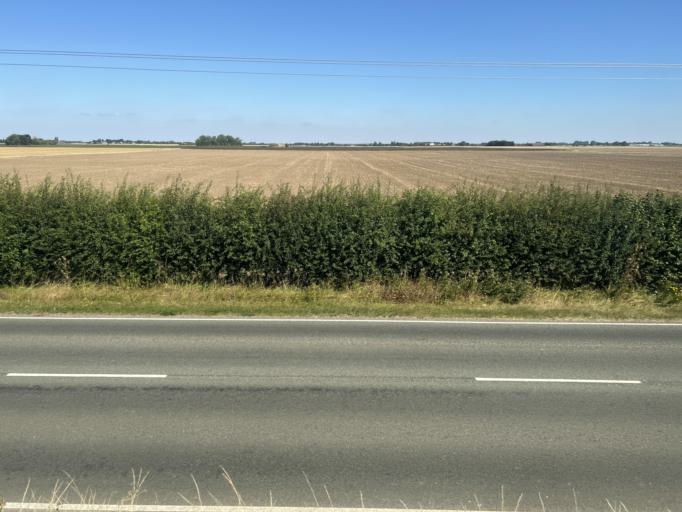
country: GB
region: England
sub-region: Lincolnshire
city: Kirton
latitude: 52.9744
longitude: -0.0945
